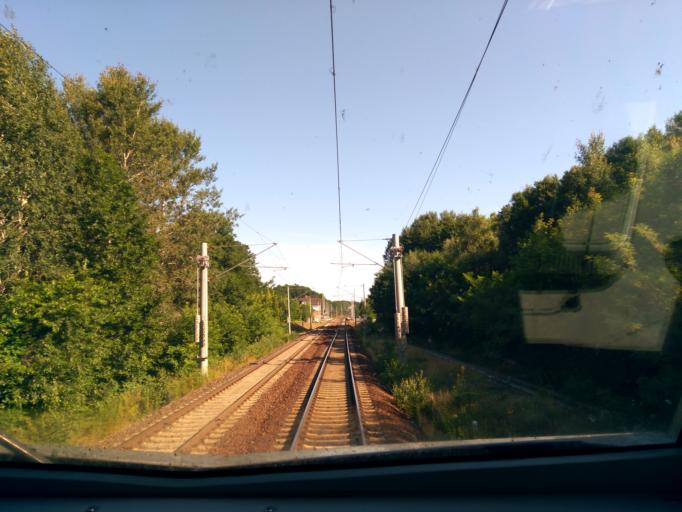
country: DE
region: Brandenburg
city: Gross Koris
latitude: 52.1572
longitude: 13.6520
